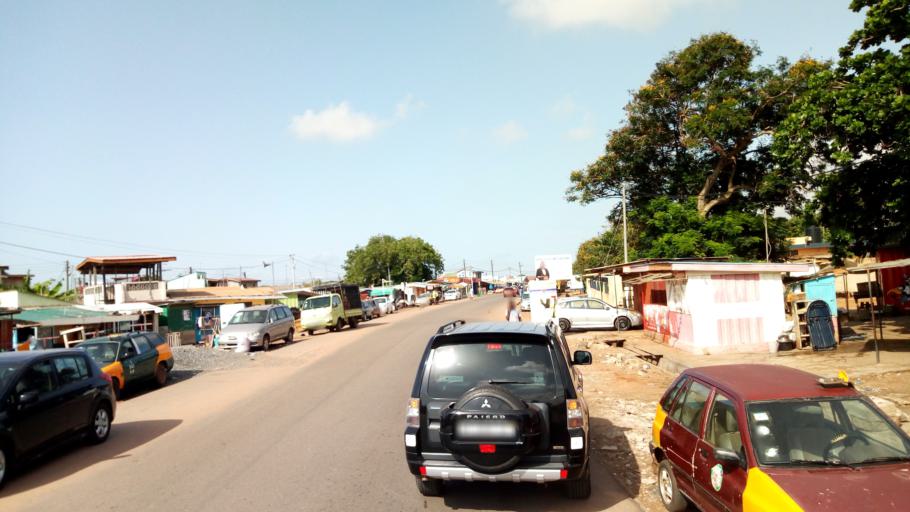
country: GH
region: Greater Accra
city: Tema
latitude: 5.6439
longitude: -0.0018
